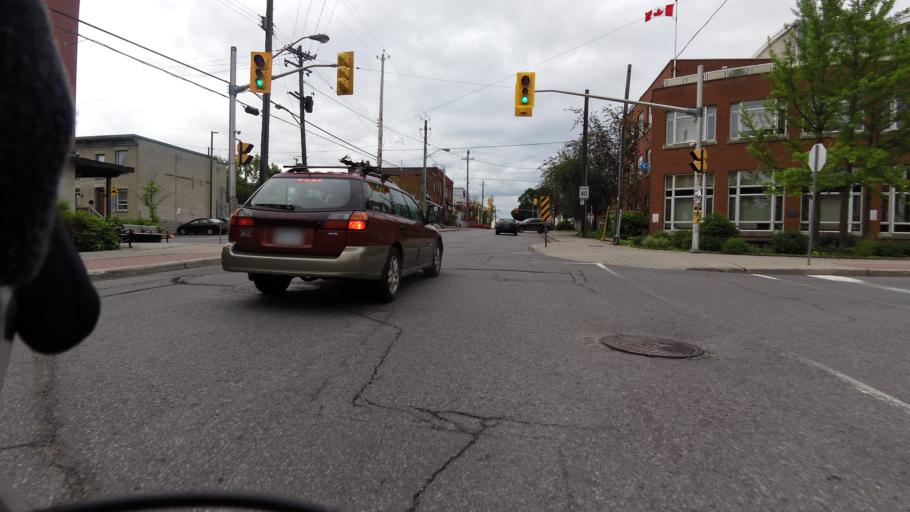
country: CA
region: Ontario
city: Ottawa
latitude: 45.4085
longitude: -75.7099
